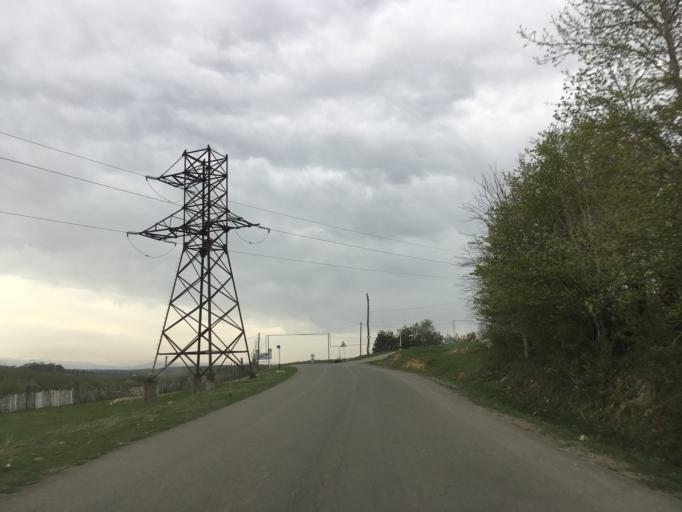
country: GE
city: Surami
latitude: 42.2091
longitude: 43.4134
